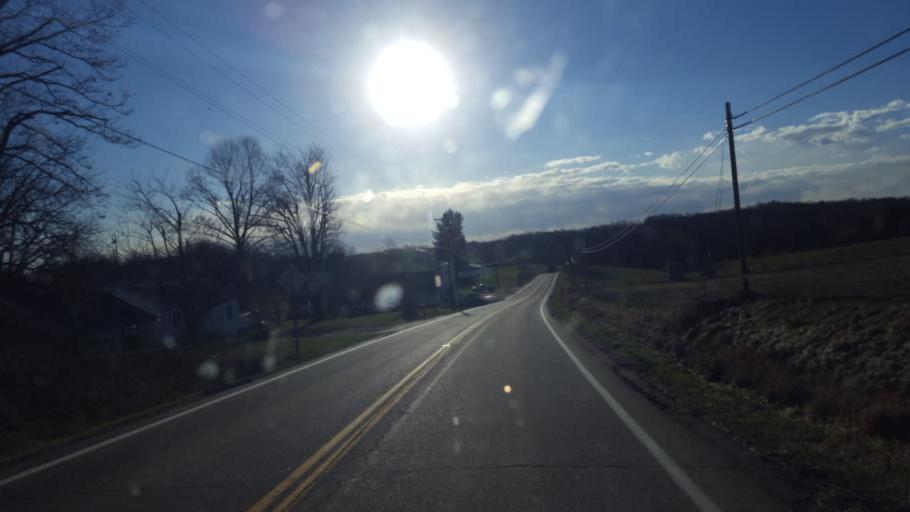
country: US
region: Ohio
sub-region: Wayne County
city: Shreve
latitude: 40.5864
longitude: -82.0646
